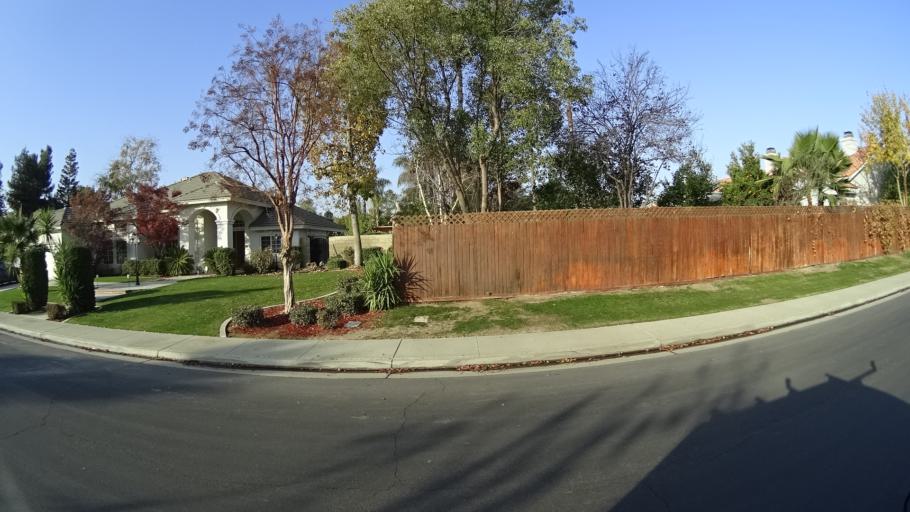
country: US
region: California
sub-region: Kern County
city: Rosedale
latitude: 35.3715
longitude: -119.1436
